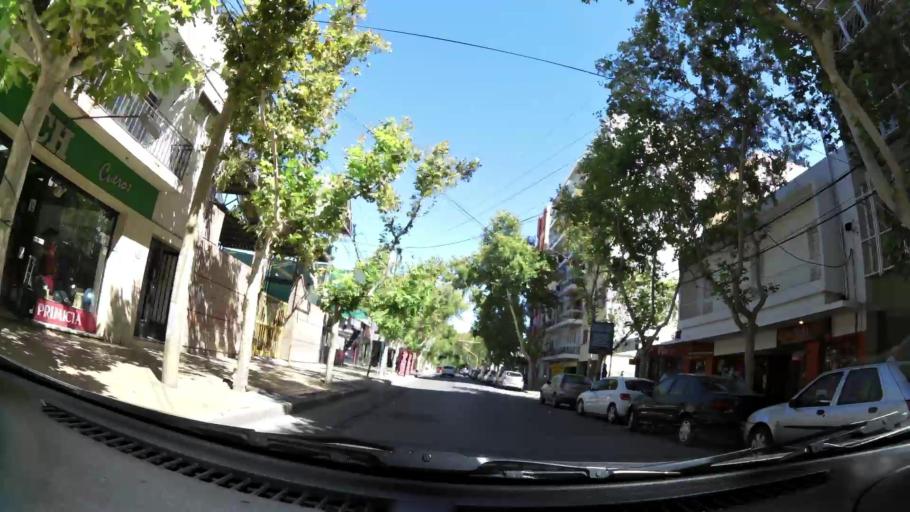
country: AR
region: San Juan
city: San Juan
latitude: -31.5369
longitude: -68.5292
